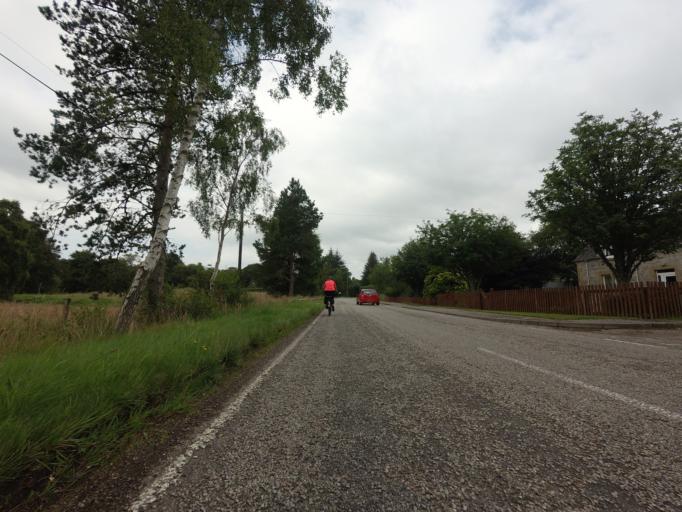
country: GB
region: Scotland
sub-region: Highland
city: Evanton
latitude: 57.9420
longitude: -4.4071
